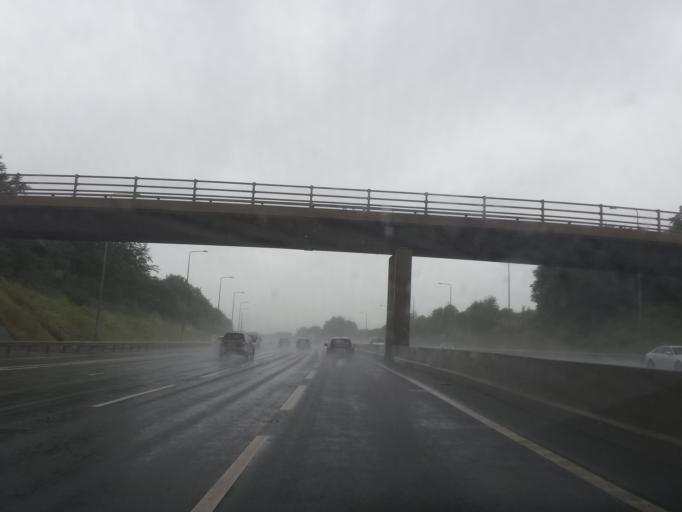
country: GB
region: England
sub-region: Nottinghamshire
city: Kimberley
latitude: 52.9830
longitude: -1.2448
